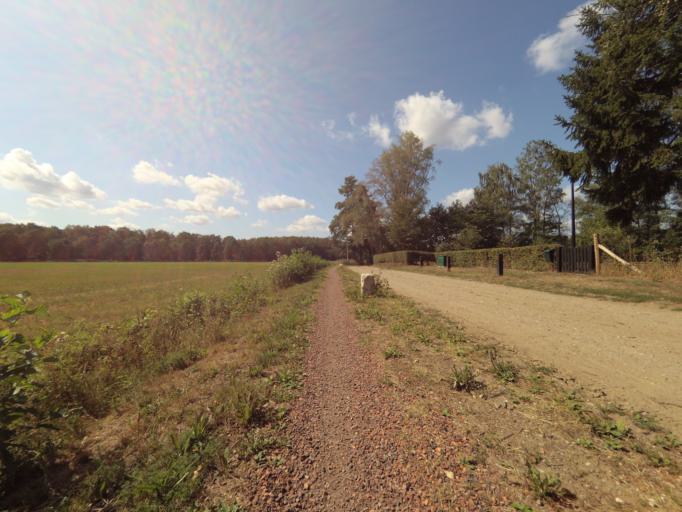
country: NL
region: Overijssel
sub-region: Gemeente Hengelo
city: Hengelo
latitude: 52.2561
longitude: 6.8407
